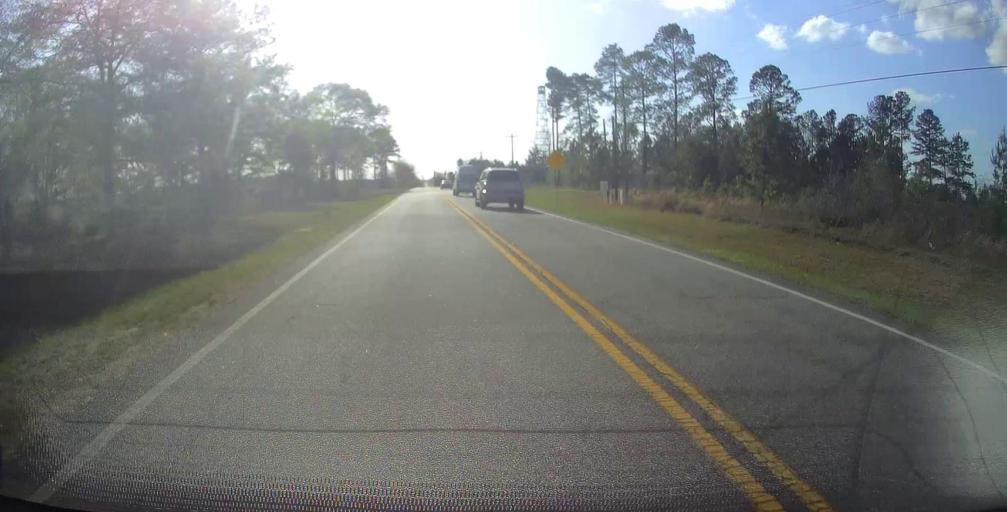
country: US
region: Georgia
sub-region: Wheeler County
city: Alamo
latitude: 32.1589
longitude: -82.7408
